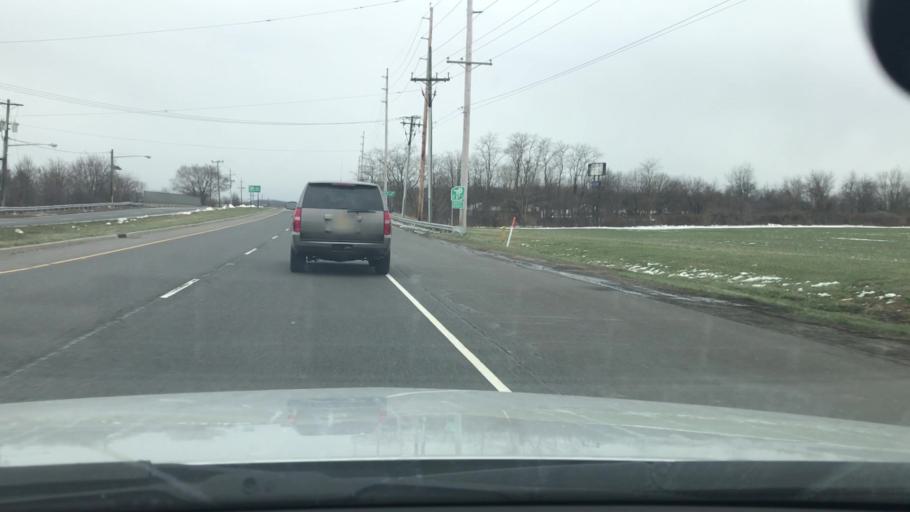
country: US
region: New Jersey
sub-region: Burlington County
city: Willingboro
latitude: 40.0303
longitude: -74.8203
